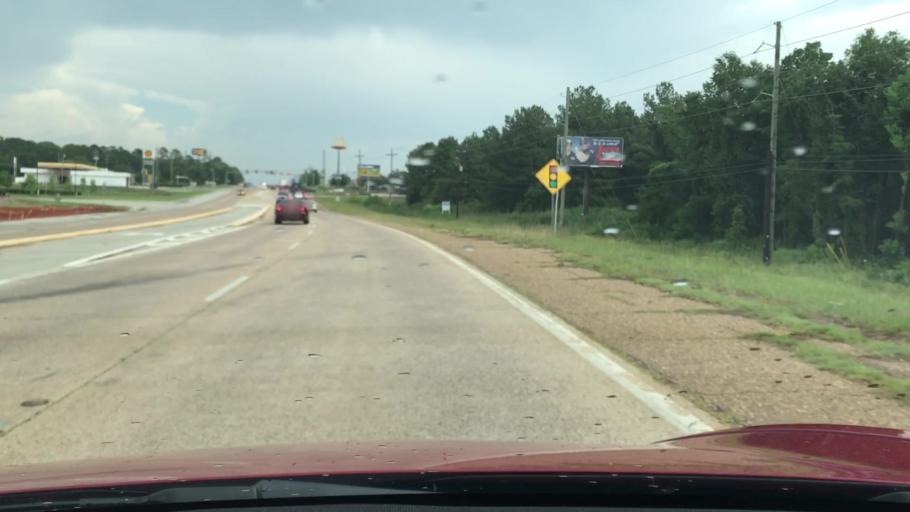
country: US
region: Louisiana
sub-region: Bossier Parish
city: Bossier City
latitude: 32.3982
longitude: -93.7670
